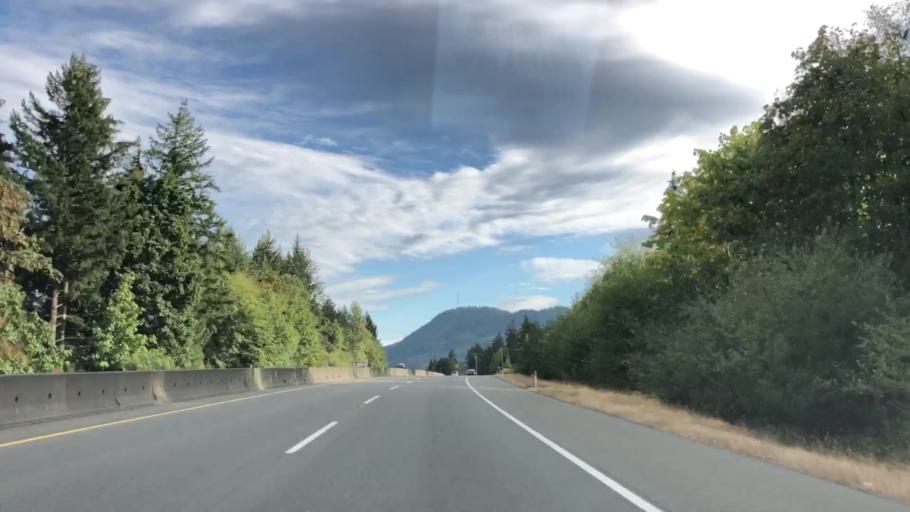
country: CA
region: British Columbia
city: North Saanich
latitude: 48.6319
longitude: -123.5491
